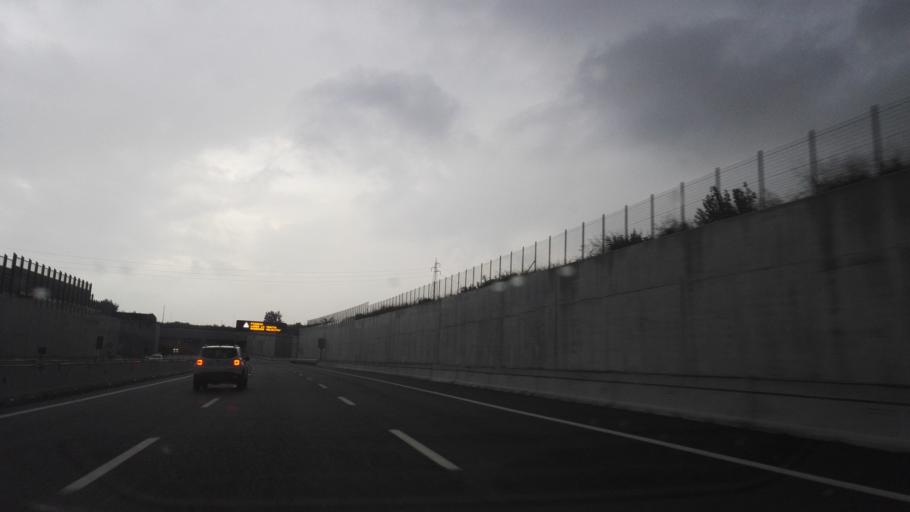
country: IT
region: Lombardy
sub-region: Citta metropolitana di Milano
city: Bellinzago Lombardo
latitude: 45.5368
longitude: 9.4367
